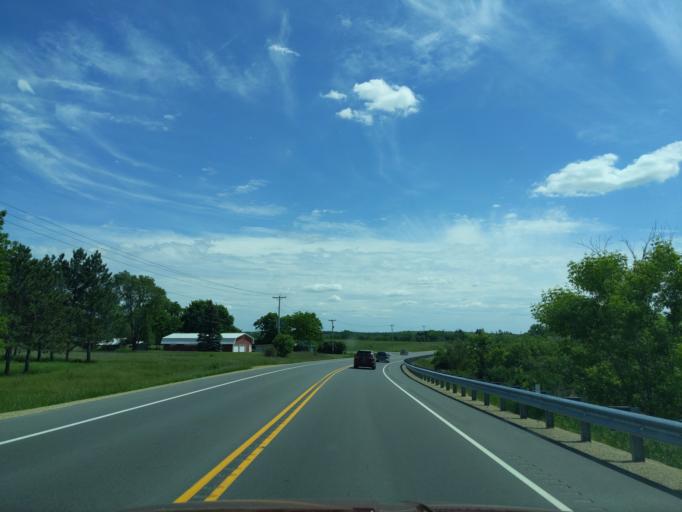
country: US
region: Wisconsin
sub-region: Columbia County
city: Pardeeville
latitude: 43.5080
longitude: -89.3063
